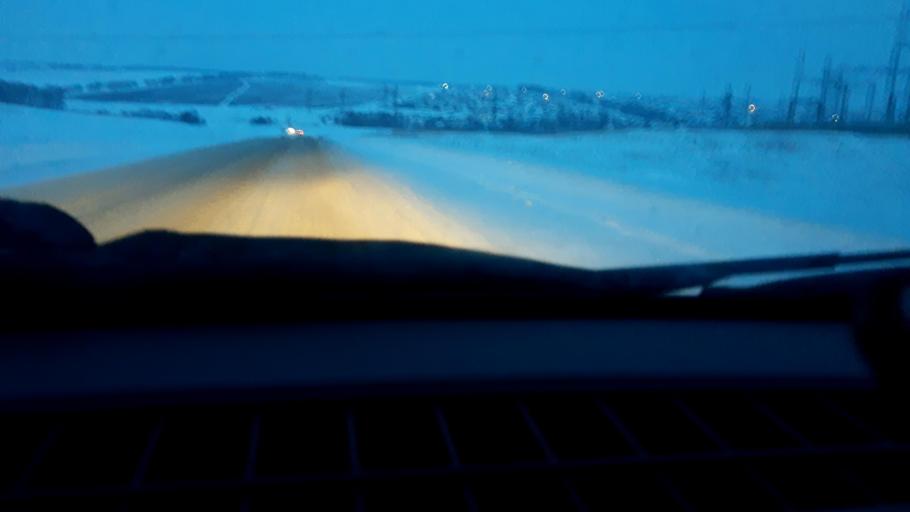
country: RU
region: Bashkortostan
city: Alekseyevka
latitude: 54.6786
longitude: 55.0162
